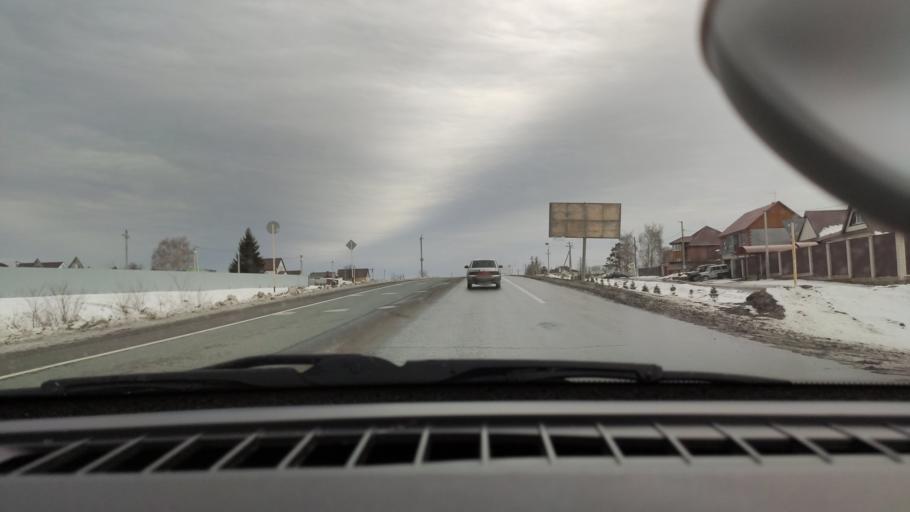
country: RU
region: Samara
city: Kurumoch
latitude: 53.4830
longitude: 50.0381
